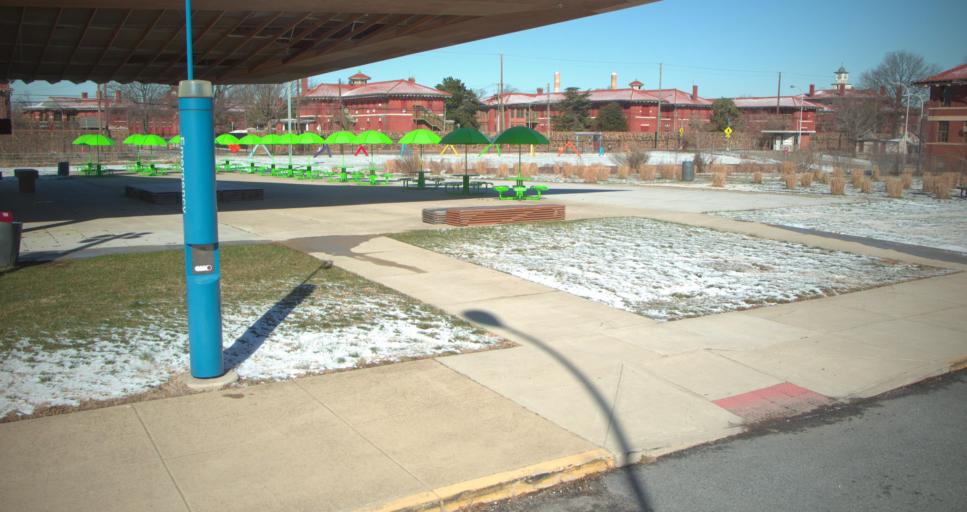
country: US
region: Maryland
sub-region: Prince George's County
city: Glassmanor
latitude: 38.8487
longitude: -76.9949
